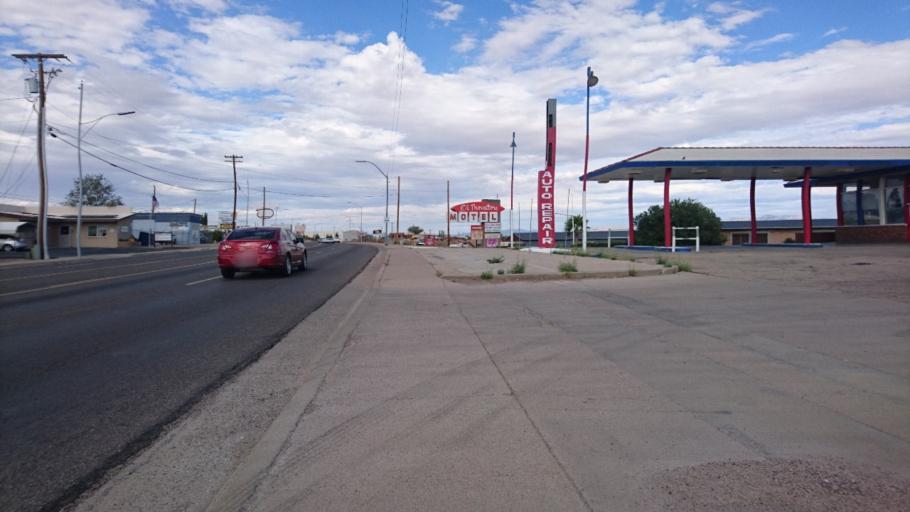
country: US
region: Arizona
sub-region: Mohave County
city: Kingman
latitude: 35.1909
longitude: -114.0349
